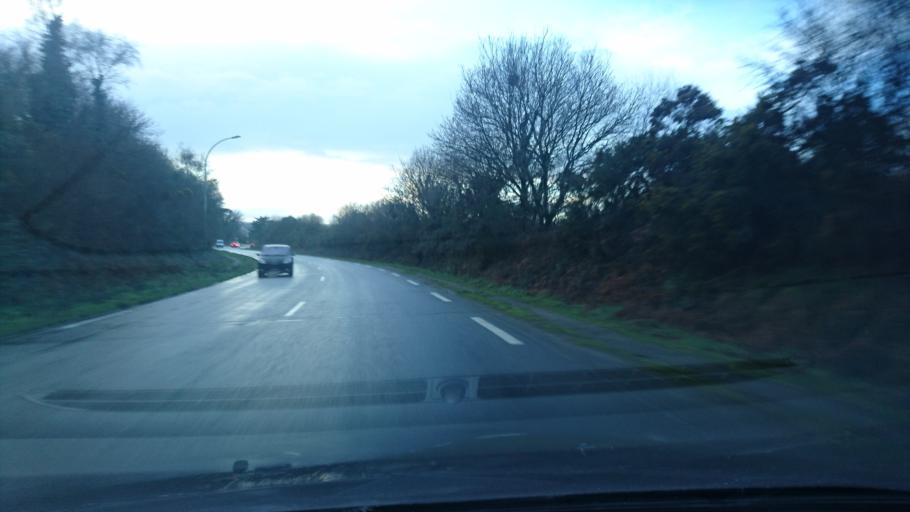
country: FR
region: Brittany
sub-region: Departement du Finistere
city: Guilers
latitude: 48.3900
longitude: -4.5334
